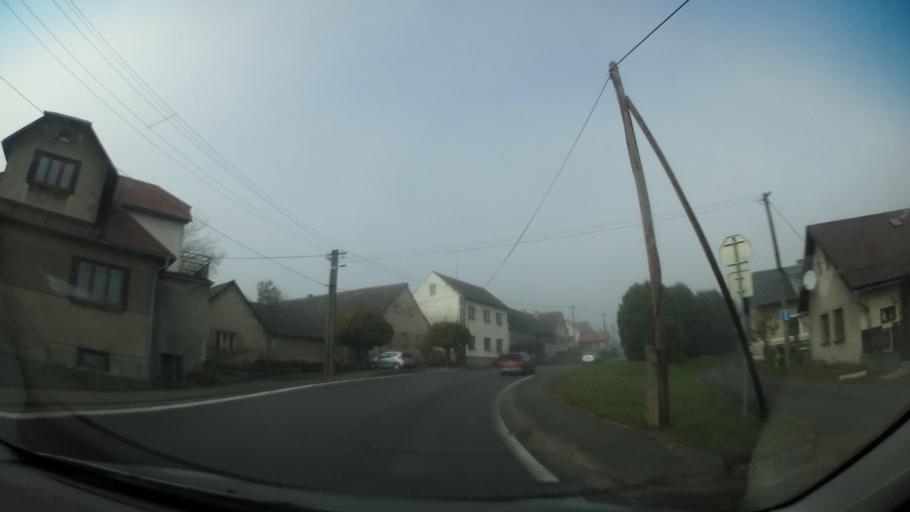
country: CZ
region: Vysocina
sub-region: Okres Zd'ar nad Sazavou
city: Nove Mesto na Morave
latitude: 49.4734
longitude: 16.0621
